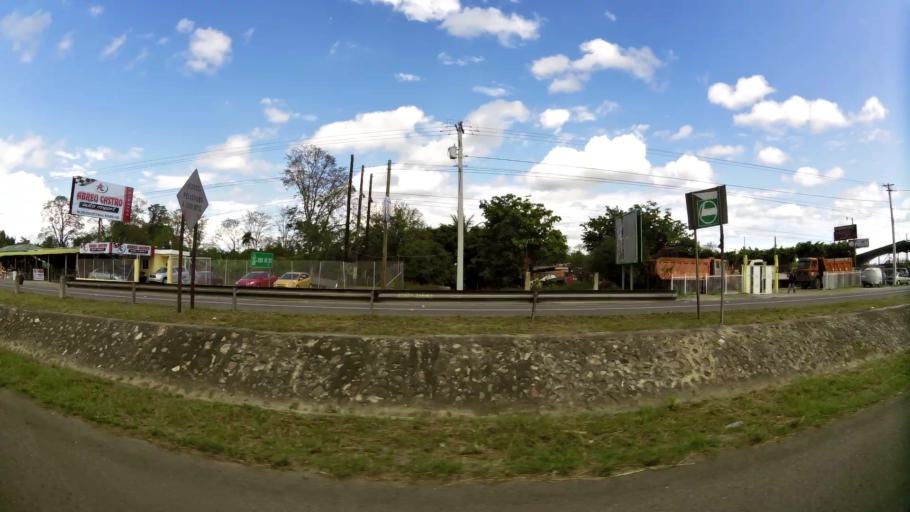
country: DO
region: La Vega
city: Rio Verde Arriba
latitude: 19.3399
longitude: -70.5993
